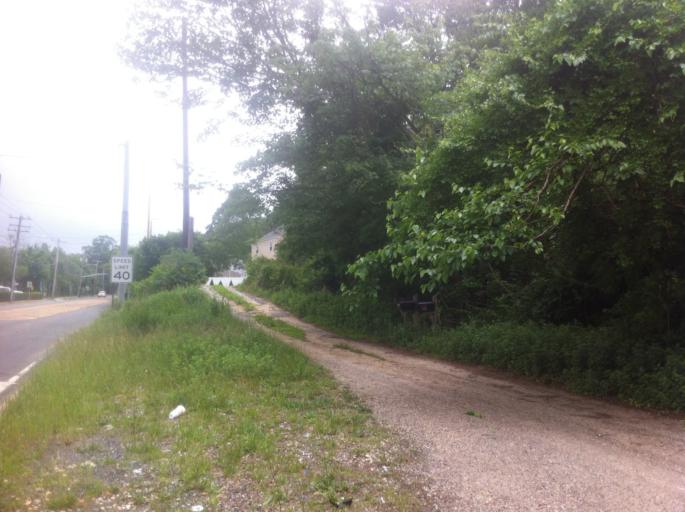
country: US
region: New York
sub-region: Nassau County
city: Oyster Bay
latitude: 40.8583
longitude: -73.5352
